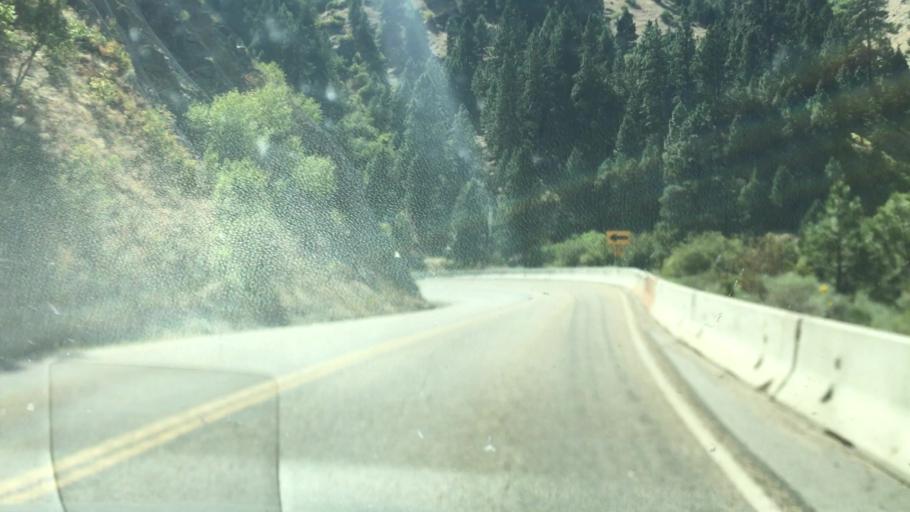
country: US
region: Idaho
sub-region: Boise County
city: Idaho City
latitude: 44.0992
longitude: -116.0983
